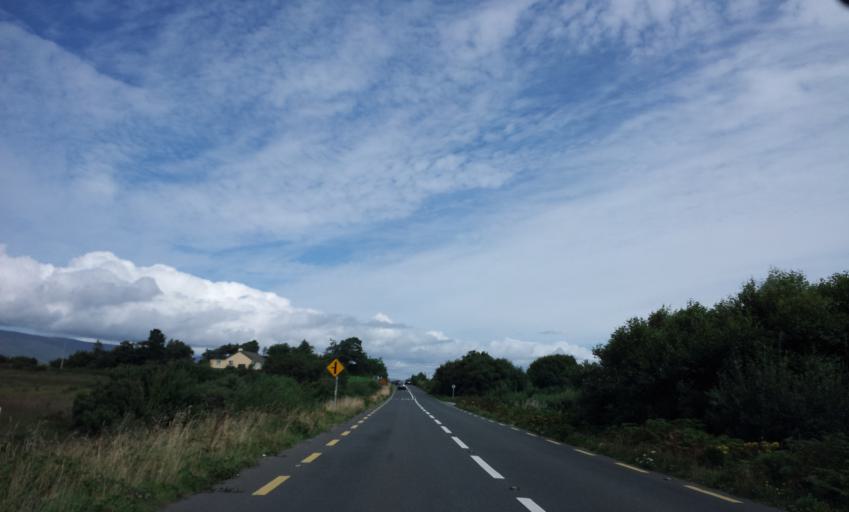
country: IE
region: Munster
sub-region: Ciarrai
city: Killorglin
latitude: 52.0895
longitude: -9.8491
